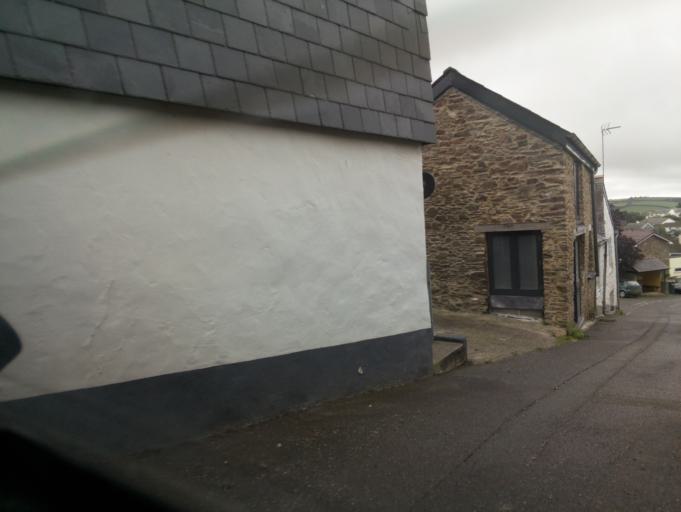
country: GB
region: England
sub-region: Devon
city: Totnes
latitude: 50.3469
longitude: -3.6786
